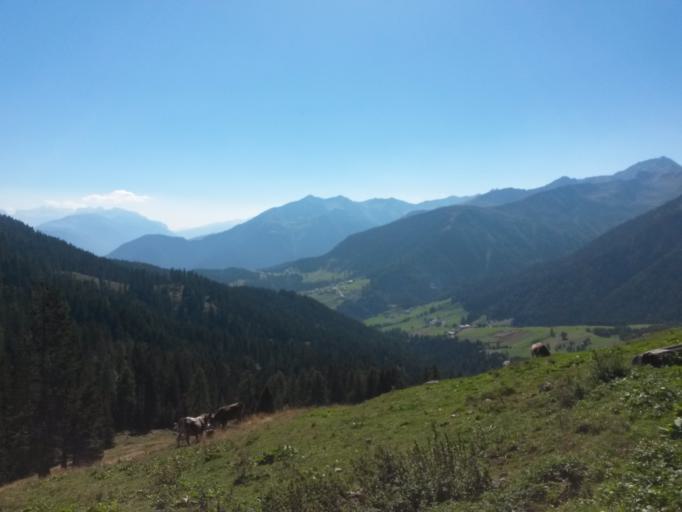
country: IT
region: Trentino-Alto Adige
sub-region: Bolzano
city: Proves - Proveis
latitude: 46.4962
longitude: 11.0521
